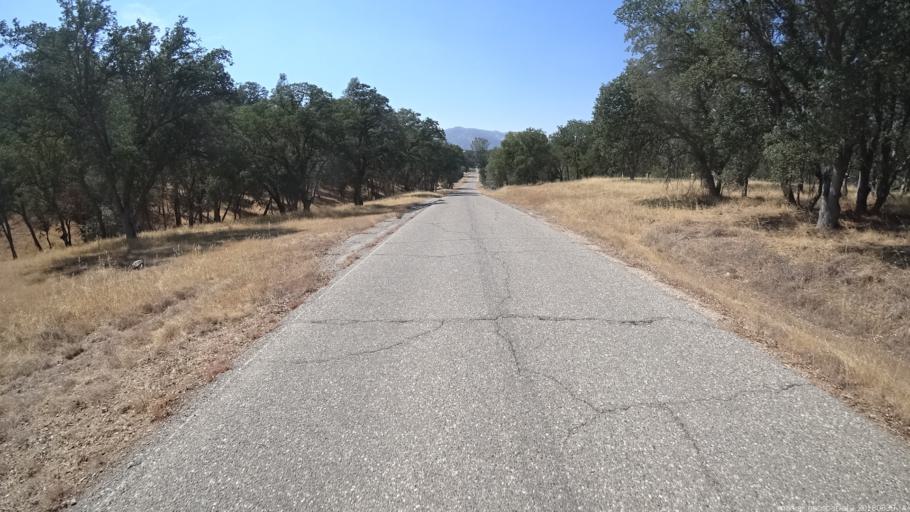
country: US
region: California
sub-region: Monterey County
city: Greenfield
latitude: 36.0815
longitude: -121.3891
